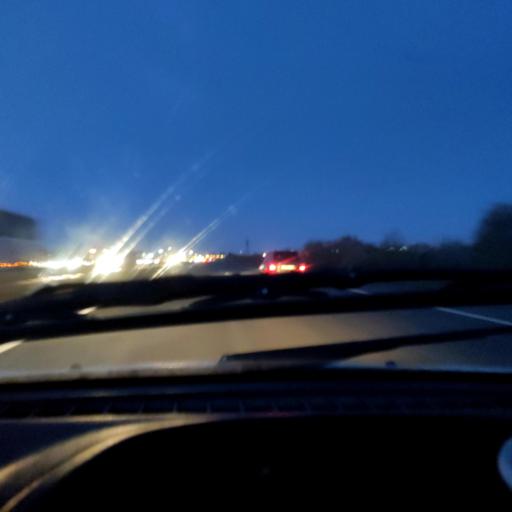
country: RU
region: Samara
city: Tol'yatti
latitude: 53.5659
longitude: 49.3715
